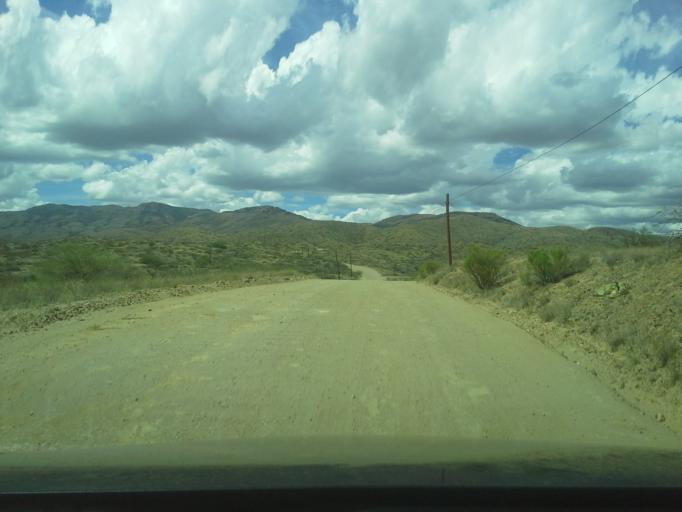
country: US
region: Arizona
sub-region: Yavapai County
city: Spring Valley
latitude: 34.2762
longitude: -112.2233
